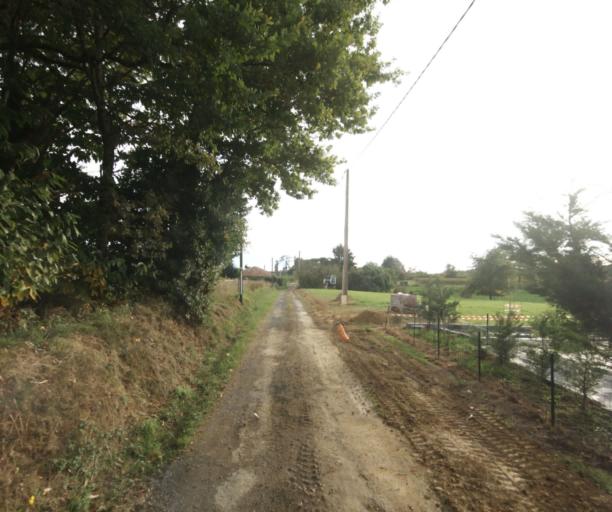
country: FR
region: Midi-Pyrenees
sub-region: Departement du Gers
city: Le Houga
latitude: 43.8581
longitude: -0.1429
